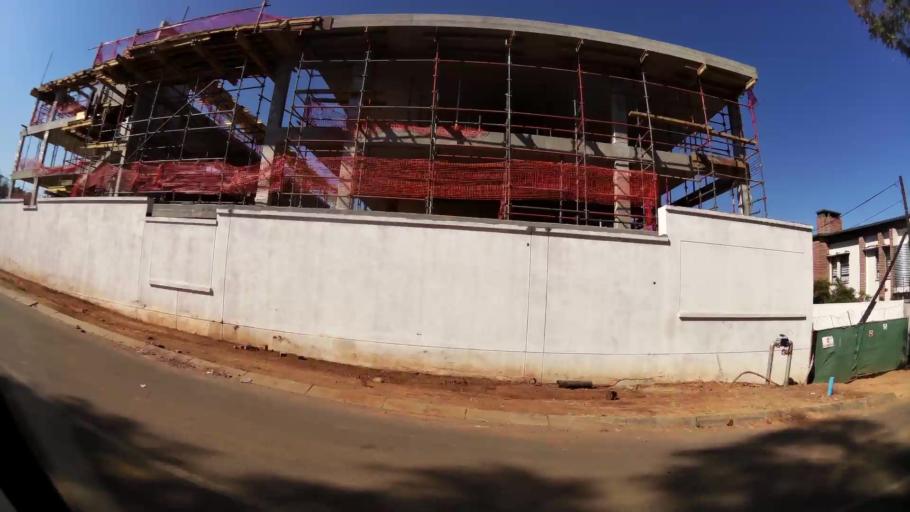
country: ZA
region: Gauteng
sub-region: City of Tshwane Metropolitan Municipality
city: Pretoria
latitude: -25.7742
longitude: 28.2637
